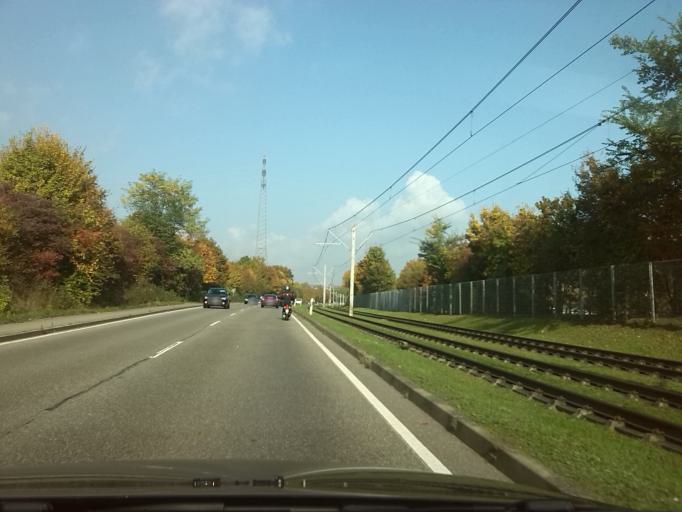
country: DE
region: Baden-Wuerttemberg
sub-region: Regierungsbezirk Stuttgart
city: Stuttgart Muehlhausen
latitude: 48.8510
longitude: 9.2445
